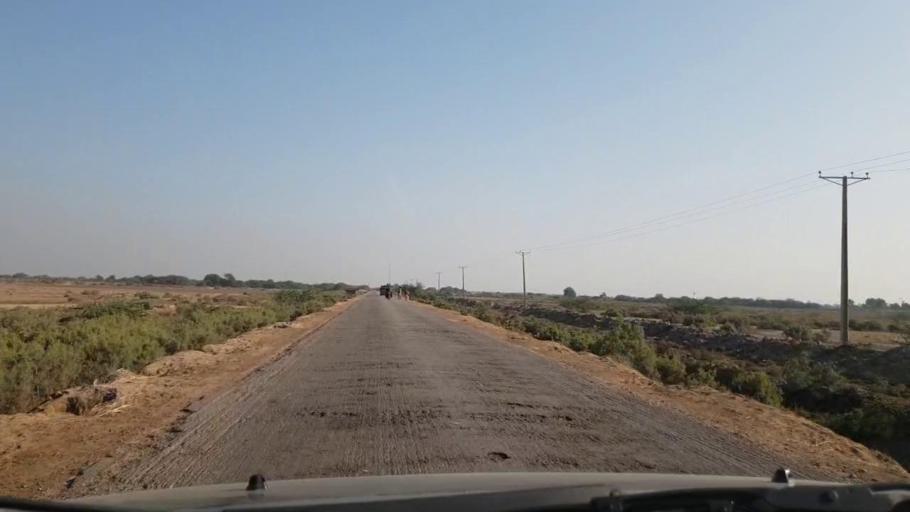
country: PK
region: Sindh
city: Tando Bago
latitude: 24.8454
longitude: 69.0313
